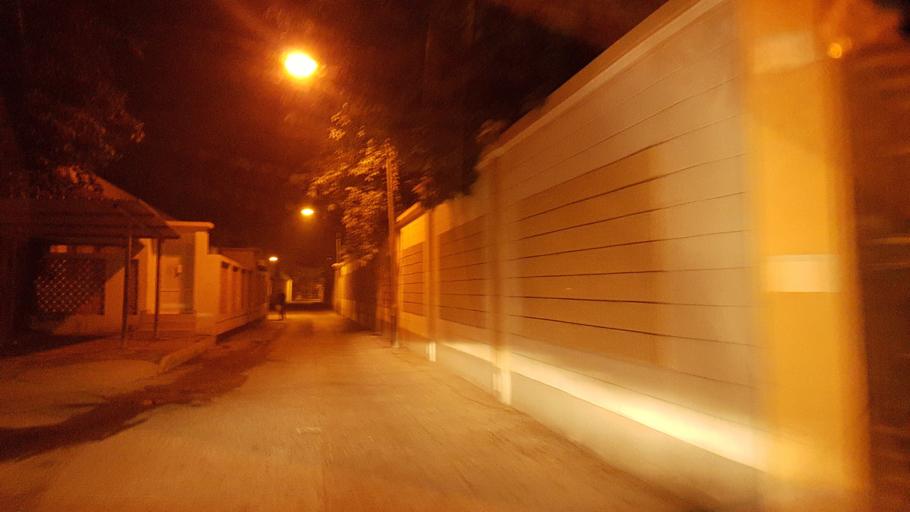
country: BH
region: Manama
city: Jidd Hafs
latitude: 26.2216
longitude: 50.4938
